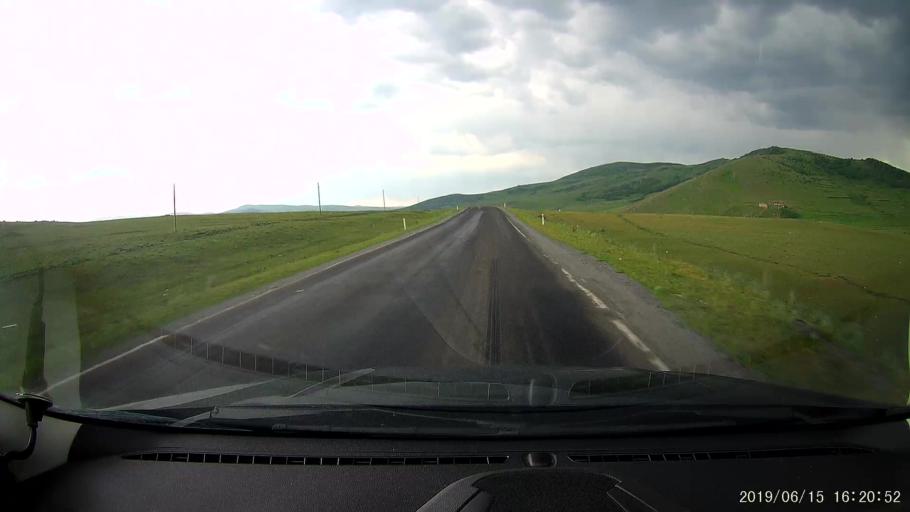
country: TR
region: Ardahan
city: Hanak
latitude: 41.2067
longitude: 42.8465
